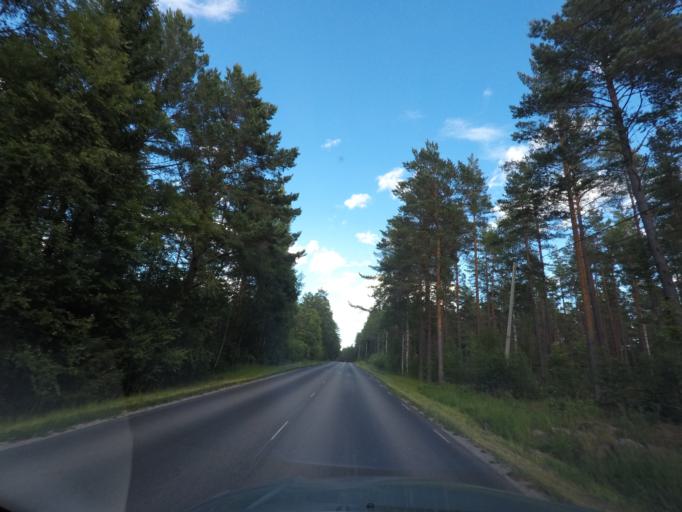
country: SE
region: Stockholm
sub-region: Sigtuna Kommun
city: Marsta
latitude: 59.6973
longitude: 17.9458
